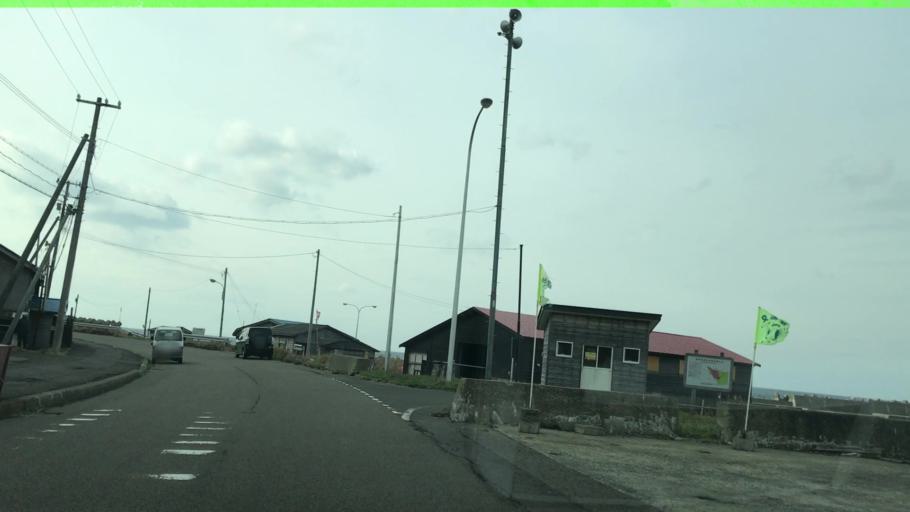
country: JP
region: Hokkaido
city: Iwanai
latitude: 43.3141
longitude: 140.3582
